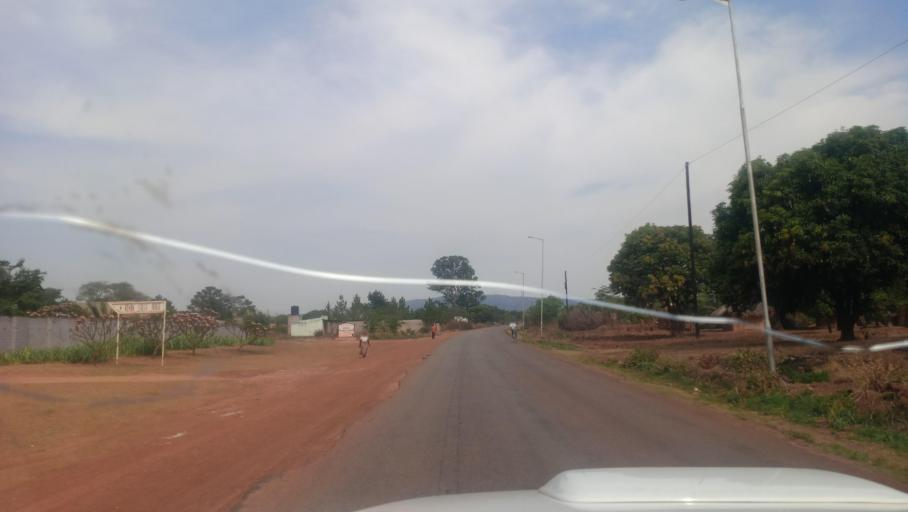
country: ZM
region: Northern
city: Mpika
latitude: -11.8332
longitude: 31.4224
